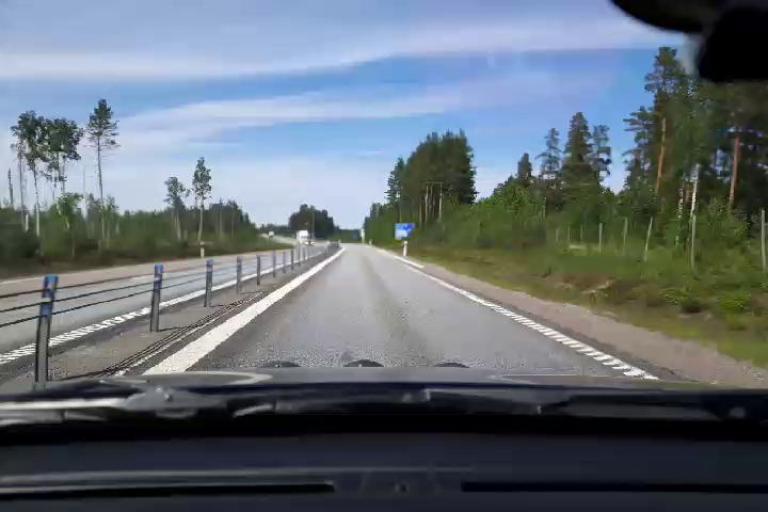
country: SE
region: Gaevleborg
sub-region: Gavle Kommun
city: Norrsundet
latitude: 61.0657
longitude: 16.9647
